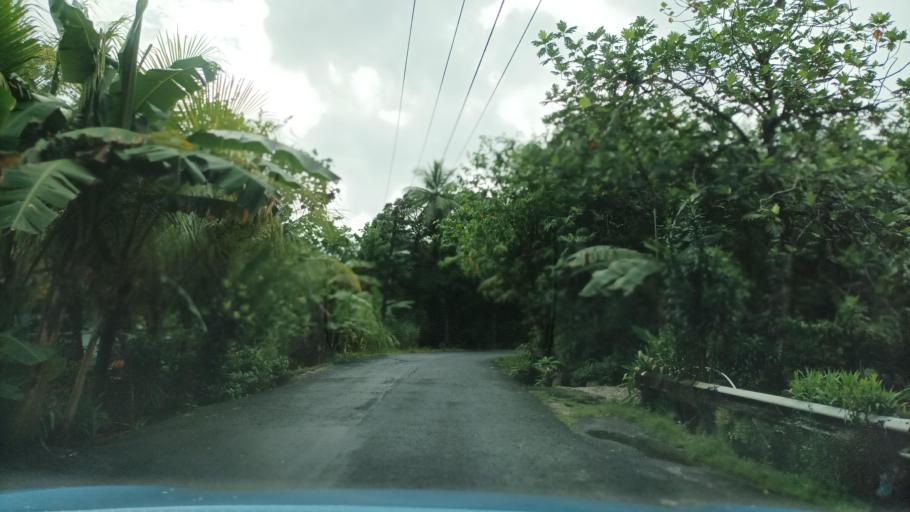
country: FM
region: Pohnpei
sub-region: Kolonia Municipality
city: Kolonia
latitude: 6.9403
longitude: 158.2773
